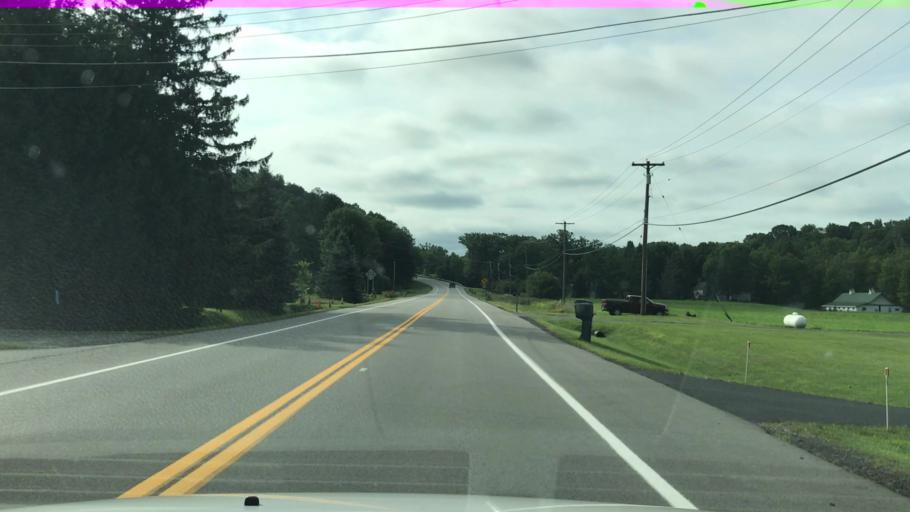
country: US
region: New York
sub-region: Erie County
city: Alden
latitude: 42.8535
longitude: -78.4938
